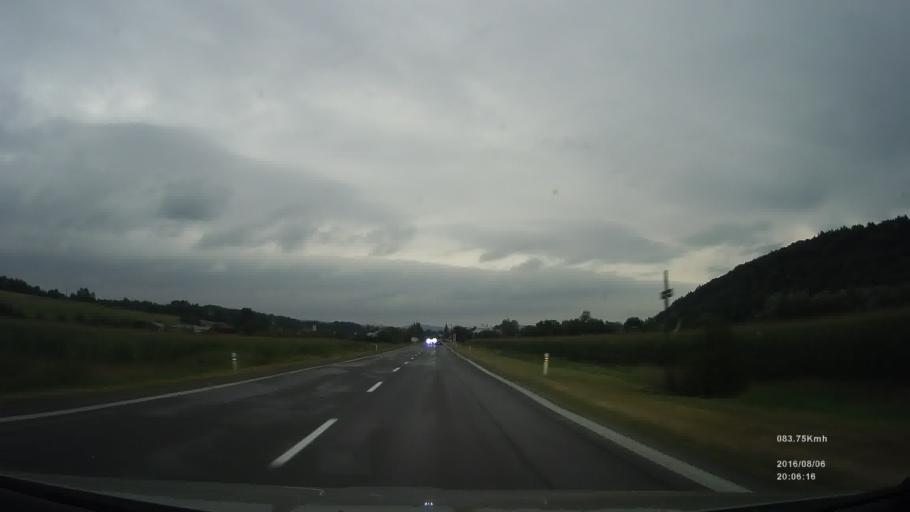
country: SK
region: Presovsky
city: Stropkov
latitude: 49.2276
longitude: 21.6318
